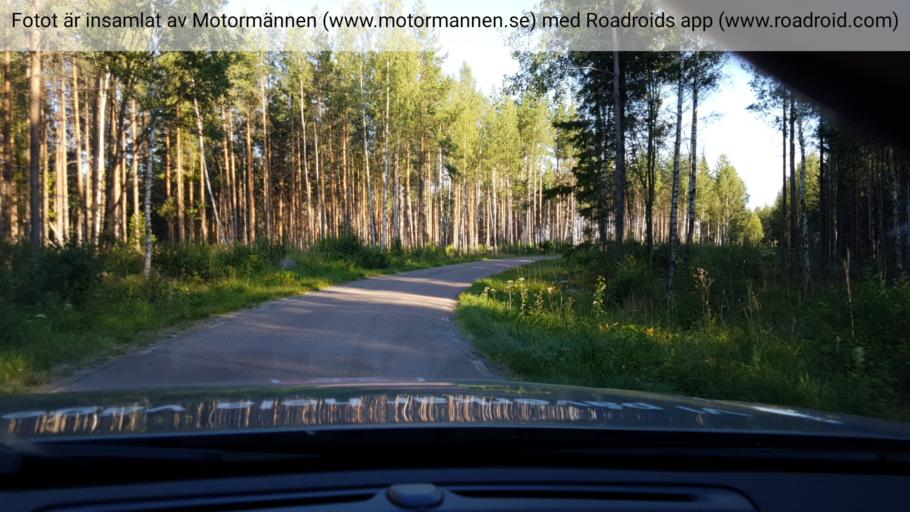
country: SE
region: Vaestmanland
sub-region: Surahammars Kommun
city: Surahammar
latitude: 59.6696
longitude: 16.0804
